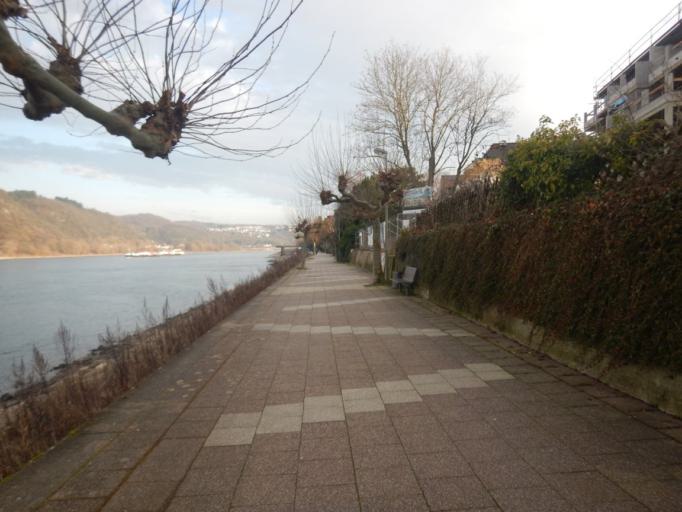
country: DE
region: Rheinland-Pfalz
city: Erpel
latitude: 50.5787
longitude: 7.2388
